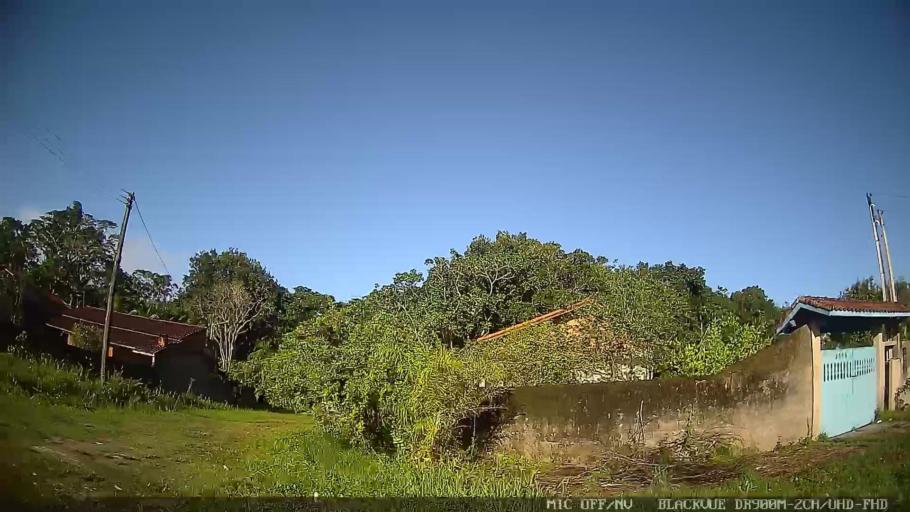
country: BR
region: Sao Paulo
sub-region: Itanhaem
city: Itanhaem
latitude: -24.2055
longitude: -46.8619
